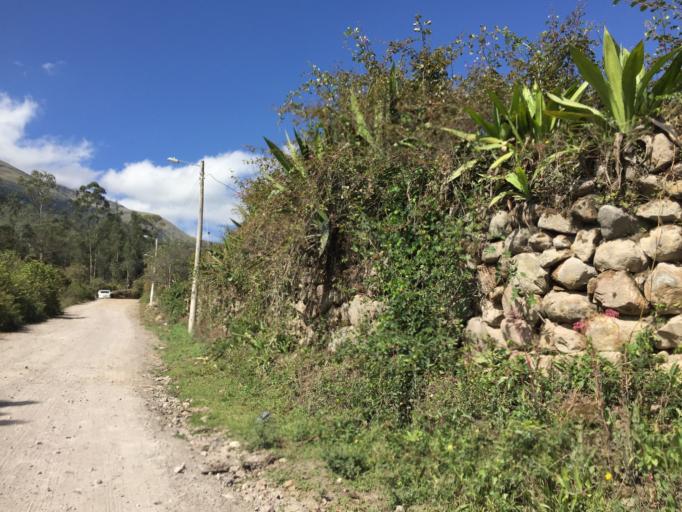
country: EC
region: Imbabura
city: Ibarra
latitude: 0.3096
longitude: -78.1500
